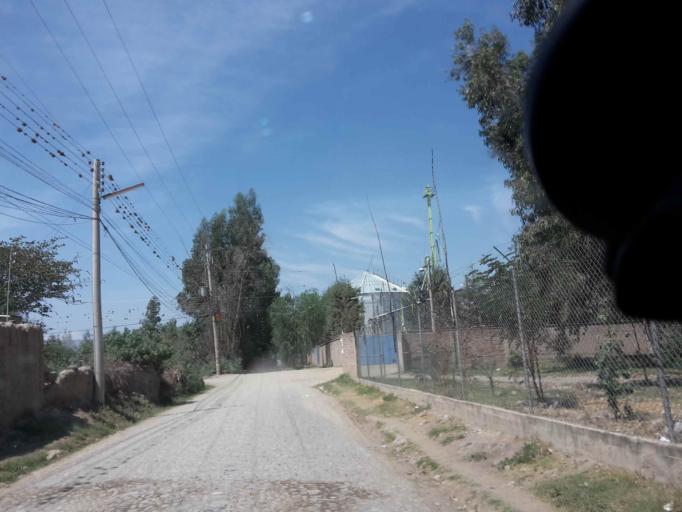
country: BO
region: Cochabamba
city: Cochabamba
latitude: -17.3542
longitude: -66.2201
